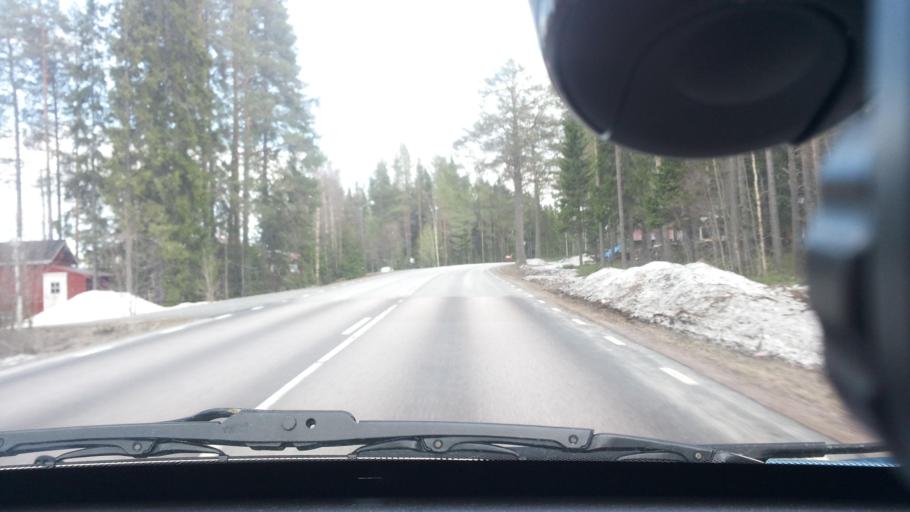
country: SE
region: Norrbotten
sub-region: Lulea Kommun
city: Gammelstad
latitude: 65.5943
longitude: 21.9981
